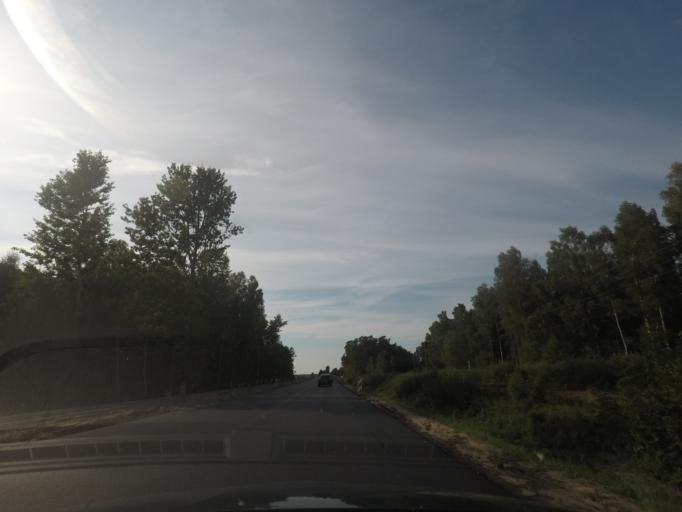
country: PL
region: Pomeranian Voivodeship
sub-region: Powiat leborski
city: Leba
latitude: 54.7323
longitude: 17.5632
